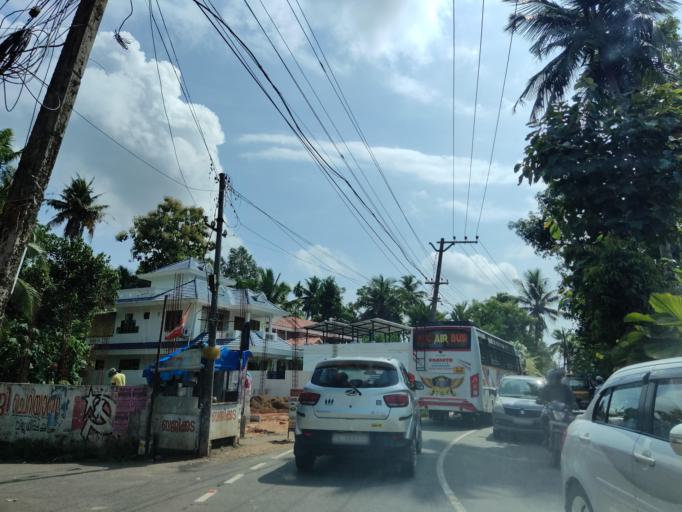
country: IN
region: Kerala
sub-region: Alappuzha
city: Mavelikara
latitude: 9.3235
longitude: 76.5224
